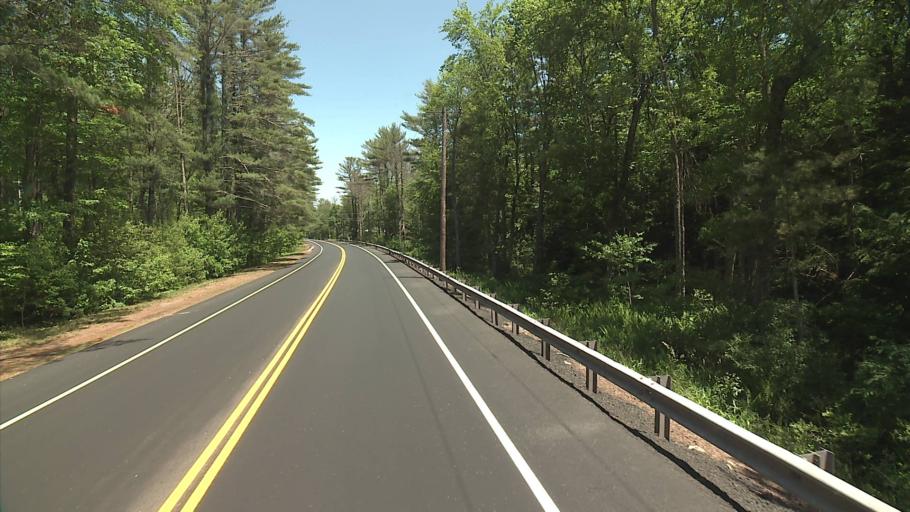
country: US
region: Connecticut
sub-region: Tolland County
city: Crystal Lake
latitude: 41.9596
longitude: -72.3660
